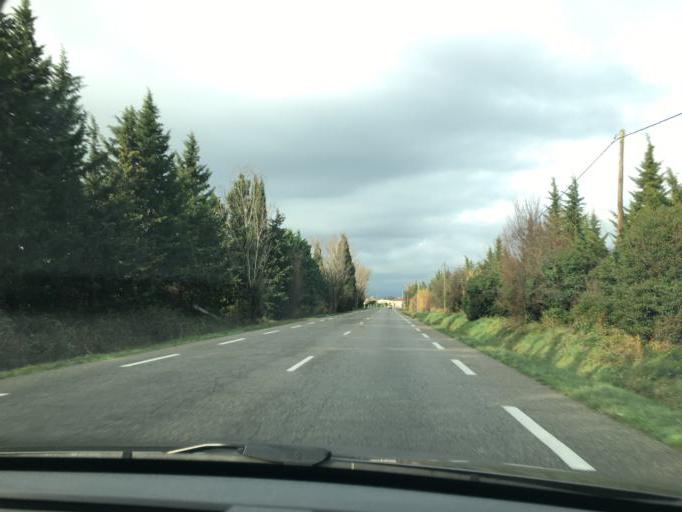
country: FR
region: Provence-Alpes-Cote d'Azur
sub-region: Departement du Vaucluse
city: L'Isle-sur-la-Sorgue
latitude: 43.8804
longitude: 5.0155
